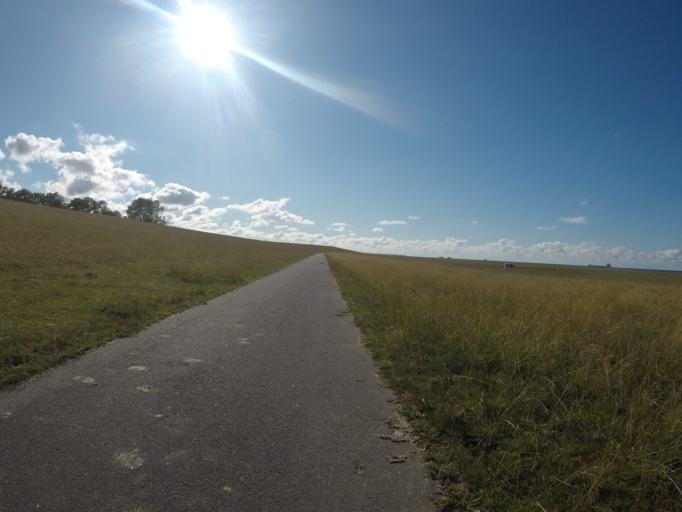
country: DE
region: Lower Saxony
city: Otterndorf
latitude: 53.8283
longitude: 8.8714
